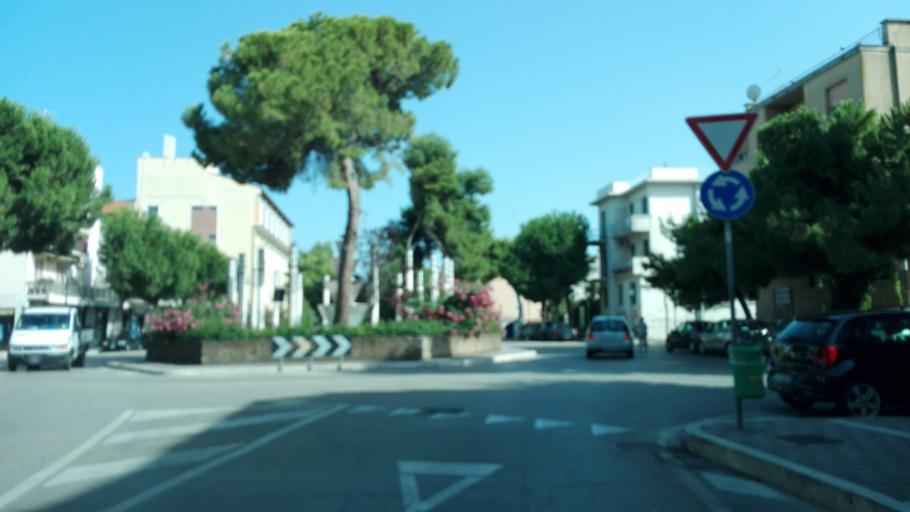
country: IT
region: Abruzzo
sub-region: Provincia di Pescara
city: Pescara
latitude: 42.4790
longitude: 14.2009
